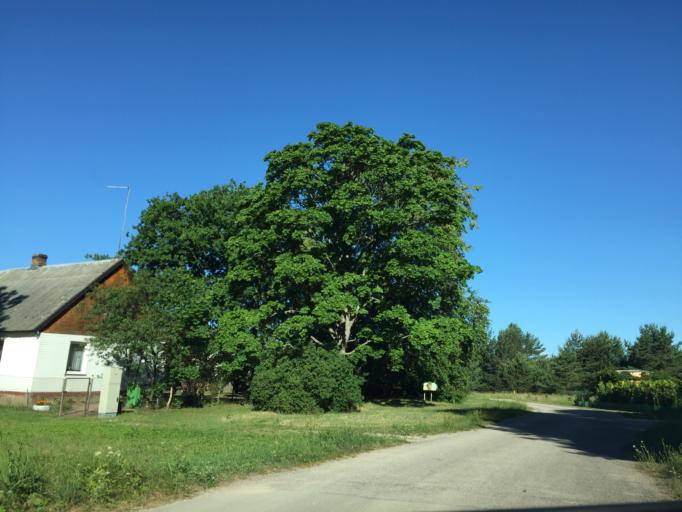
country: LV
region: Ventspils
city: Ventspils
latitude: 57.4381
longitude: 21.6128
